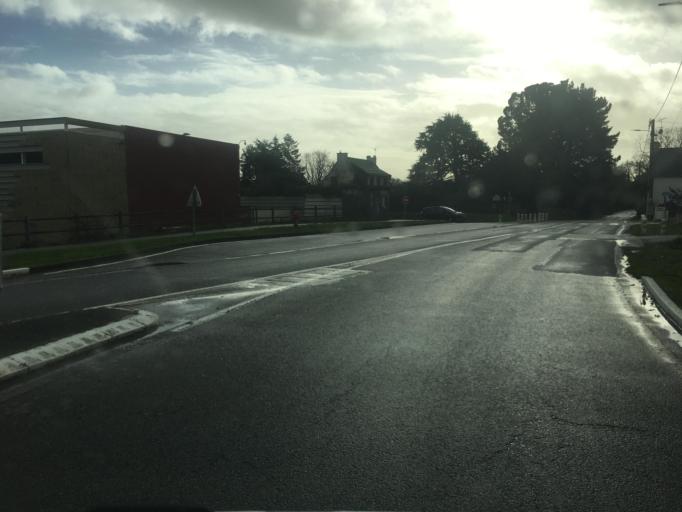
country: FR
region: Brittany
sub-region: Departement du Morbihan
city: Sarzeau
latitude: 47.5218
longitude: -2.7676
